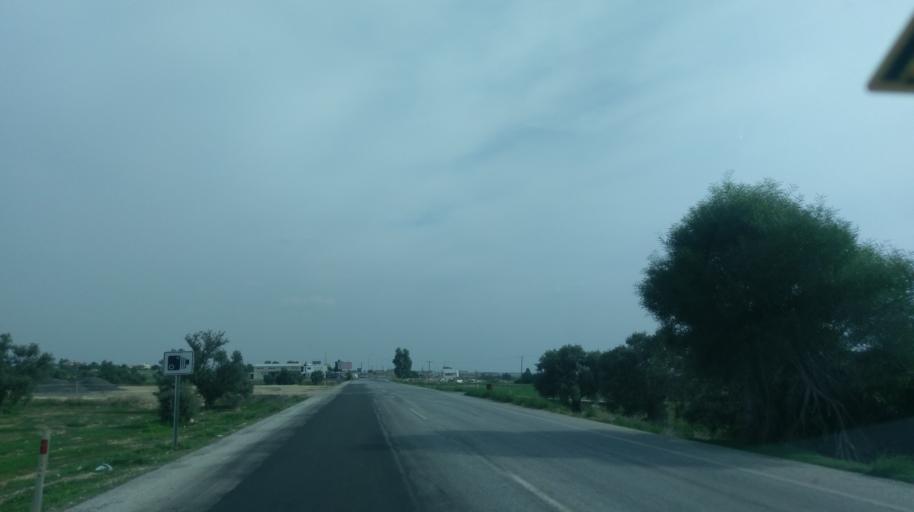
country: CY
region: Larnaka
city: Athienou
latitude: 35.2294
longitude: 33.5462
